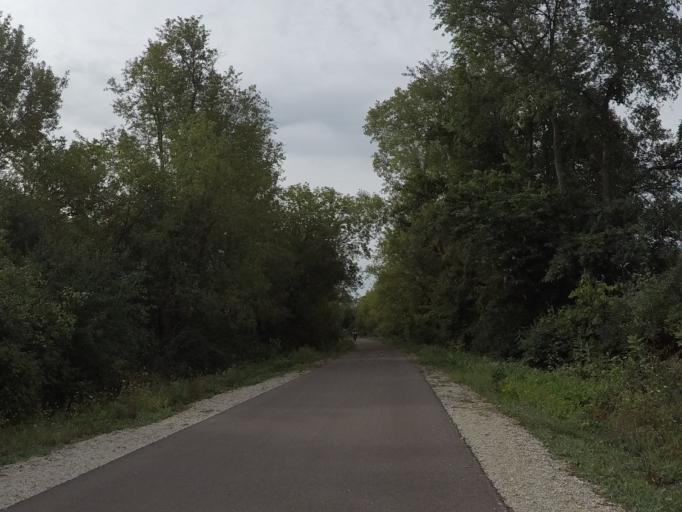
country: US
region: Wisconsin
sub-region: Sauk County
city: Prairie du Sac
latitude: 43.3337
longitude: -89.7501
